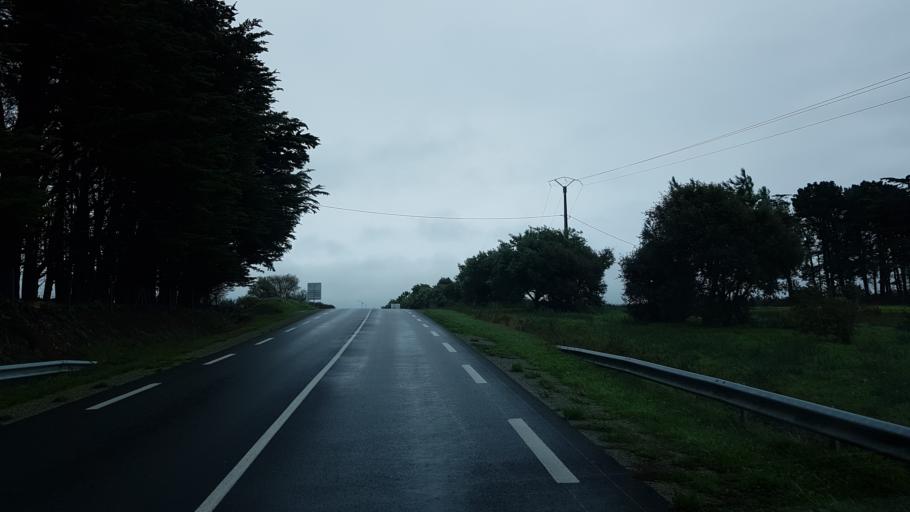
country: FR
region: Brittany
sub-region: Departement du Morbihan
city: Saint-Gildas-de-Rhuys
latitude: 47.5328
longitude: -2.8503
